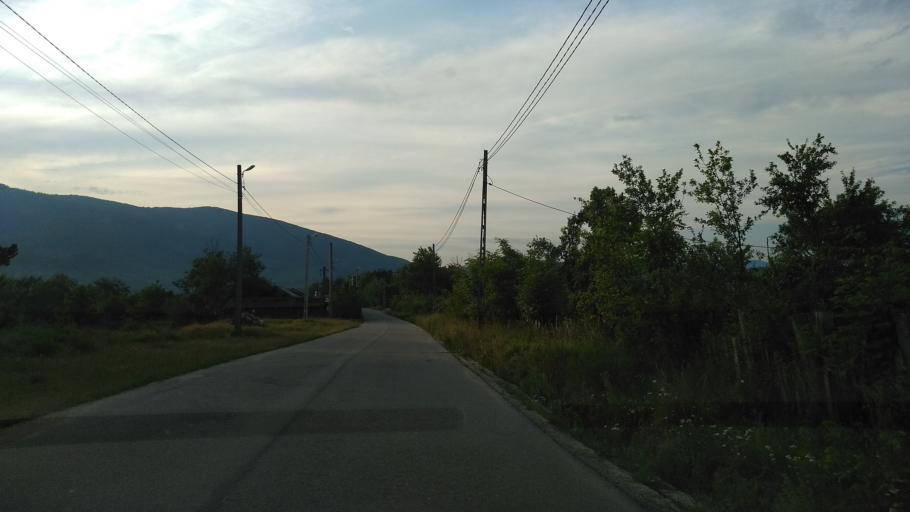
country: RO
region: Hunedoara
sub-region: Municipiul  Vulcan
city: Jiu-Paroseni
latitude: 45.3578
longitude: 23.2884
